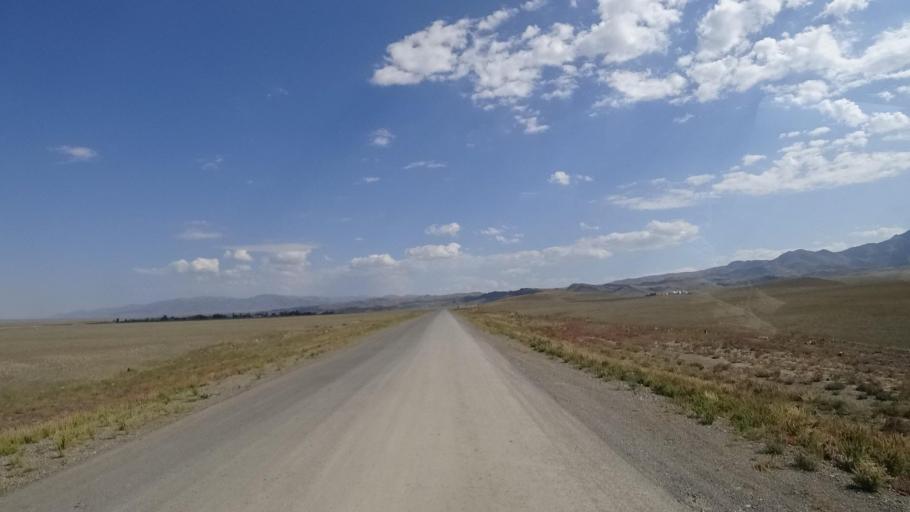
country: KZ
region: Almaty Oblysy
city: Kegen
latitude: 43.2149
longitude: 79.0908
